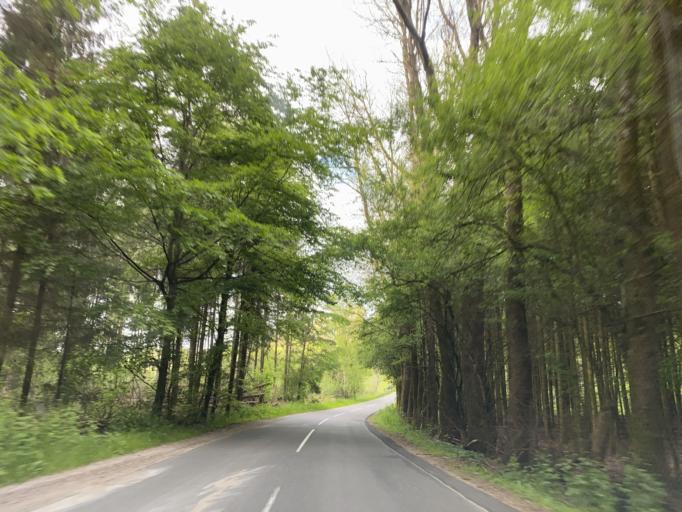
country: DK
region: Central Jutland
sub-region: Horsens Kommune
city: Braedstrup
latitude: 56.0322
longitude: 9.6564
